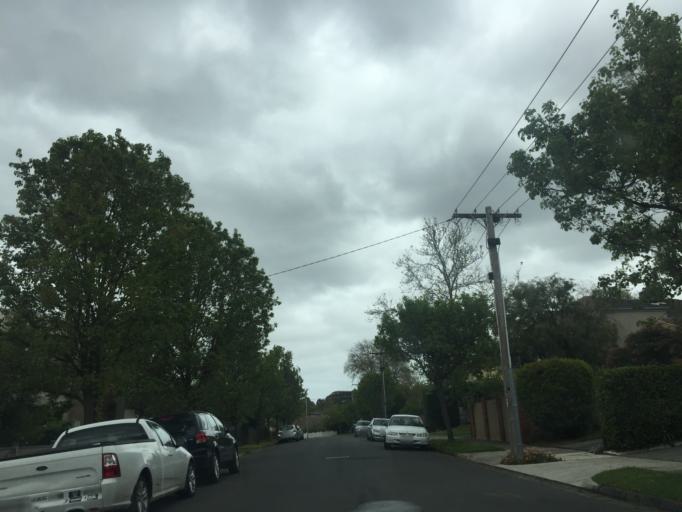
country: AU
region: Victoria
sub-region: Boroondara
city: Kew
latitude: -37.7972
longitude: 145.0396
